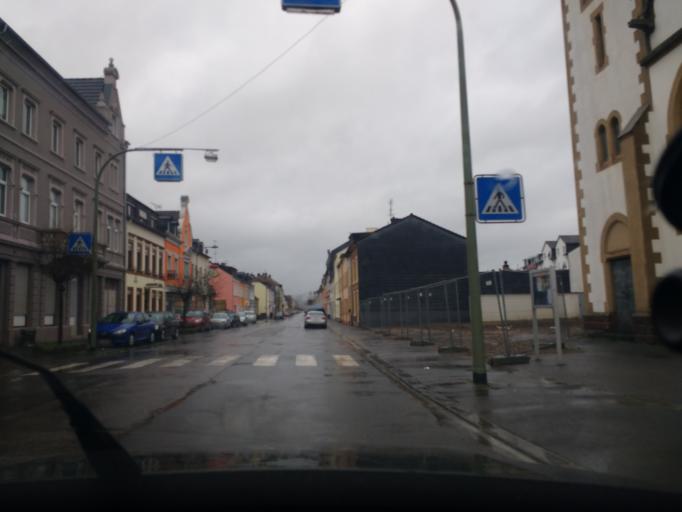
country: DE
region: Rheinland-Pfalz
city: Konz
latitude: 49.7075
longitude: 6.5860
